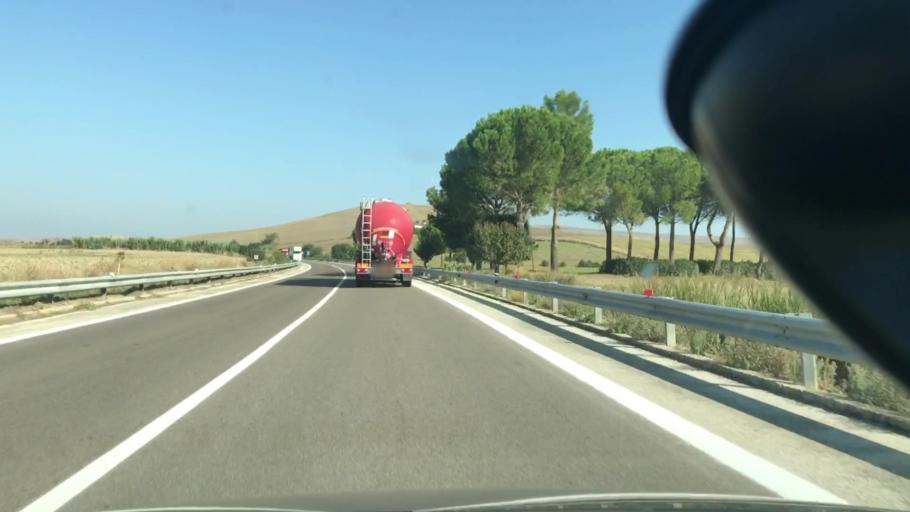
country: IT
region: Basilicate
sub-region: Provincia di Matera
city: Irsina
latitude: 40.8064
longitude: 16.2729
